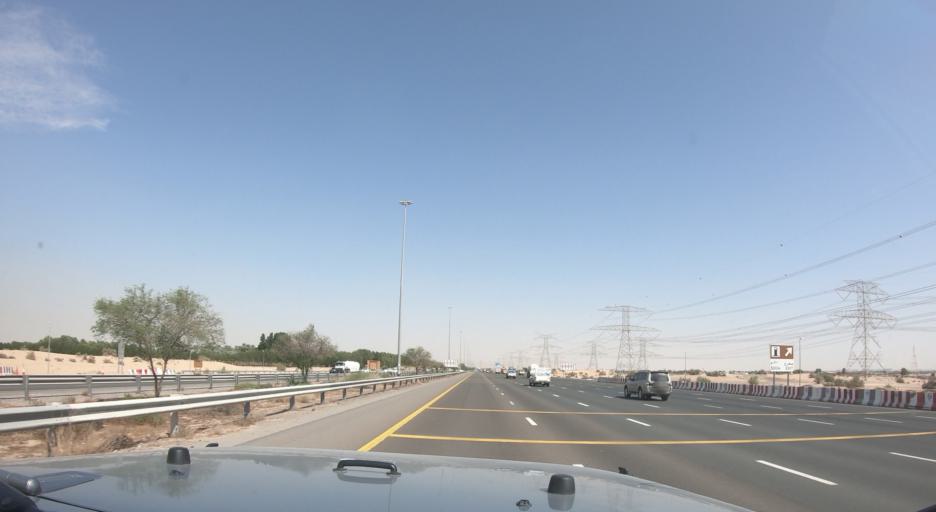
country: AE
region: Ash Shariqah
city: Sharjah
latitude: 25.1860
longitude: 55.5260
